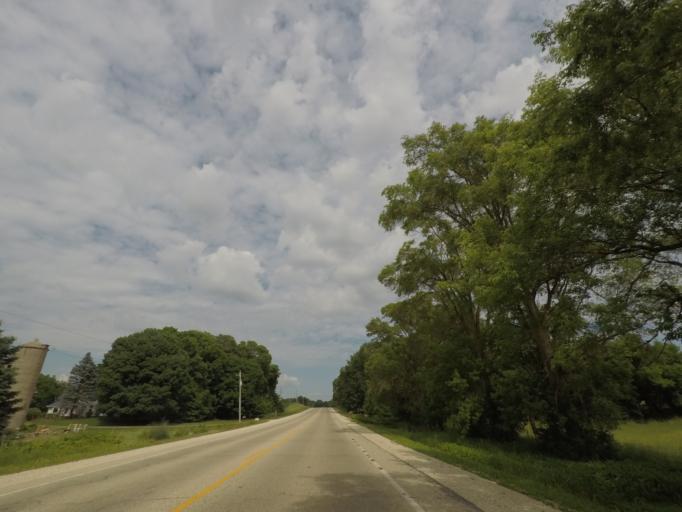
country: US
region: Wisconsin
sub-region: Rock County
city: Milton
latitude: 42.8247
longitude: -88.9703
